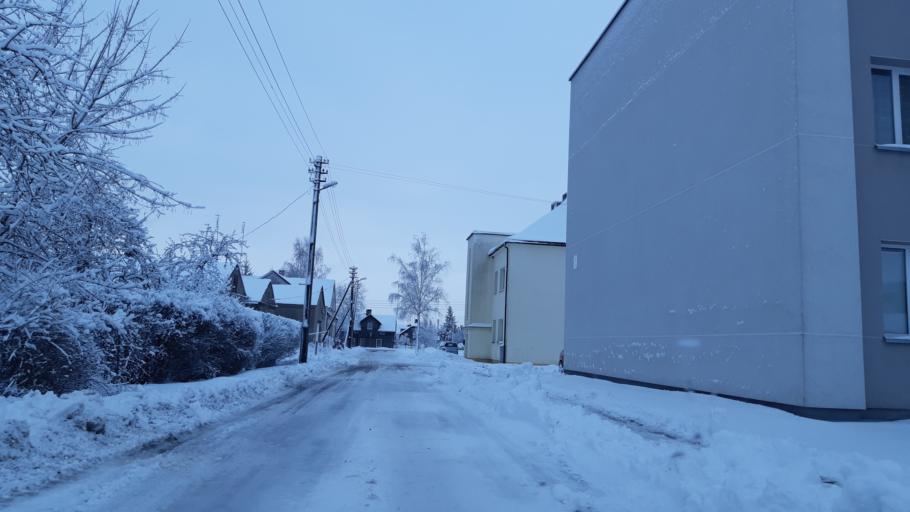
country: LT
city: Kybartai
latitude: 54.6352
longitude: 22.7570
